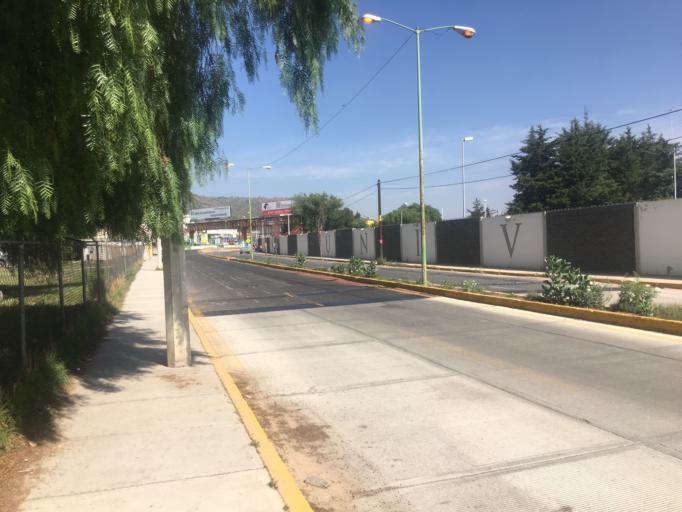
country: MX
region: Hidalgo
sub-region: Mineral de la Reforma
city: Carboneras
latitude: 20.0932
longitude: -98.7129
